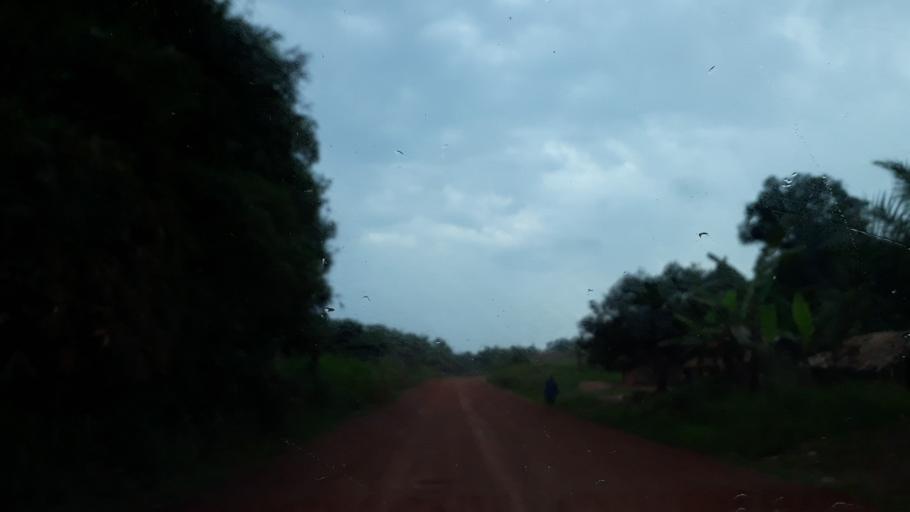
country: CD
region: Eastern Province
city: Kisangani
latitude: 0.4699
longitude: 25.4310
